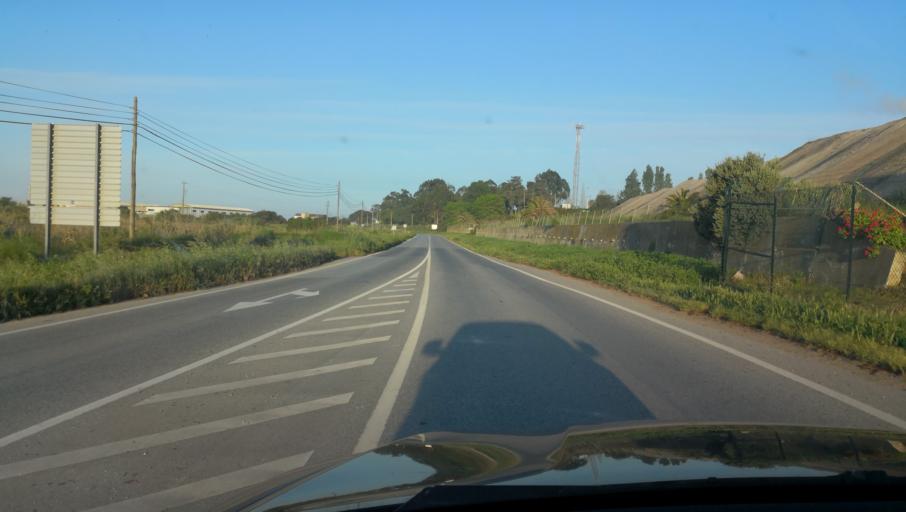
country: PT
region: Setubal
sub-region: Setubal
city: Setubal
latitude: 38.4903
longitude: -8.8021
